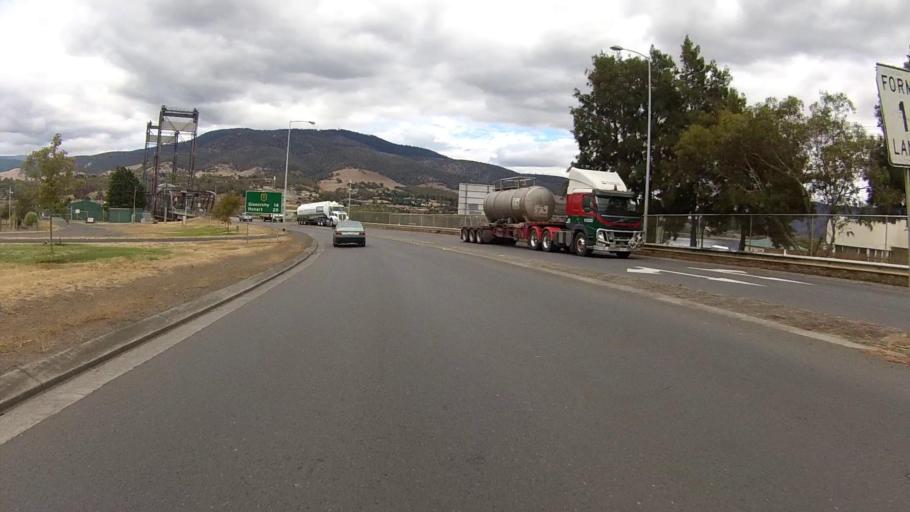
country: AU
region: Tasmania
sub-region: Brighton
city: Bridgewater
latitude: -42.7386
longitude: 147.2268
